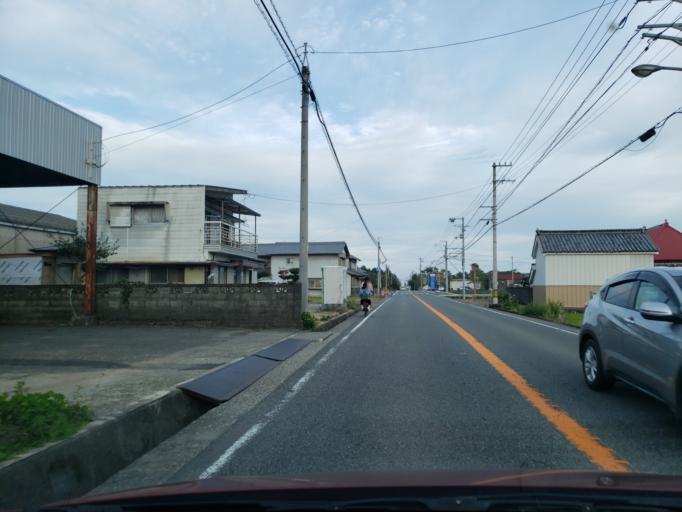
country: JP
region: Tokushima
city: Kamojimacho-jogejima
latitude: 34.0807
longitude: 134.2597
